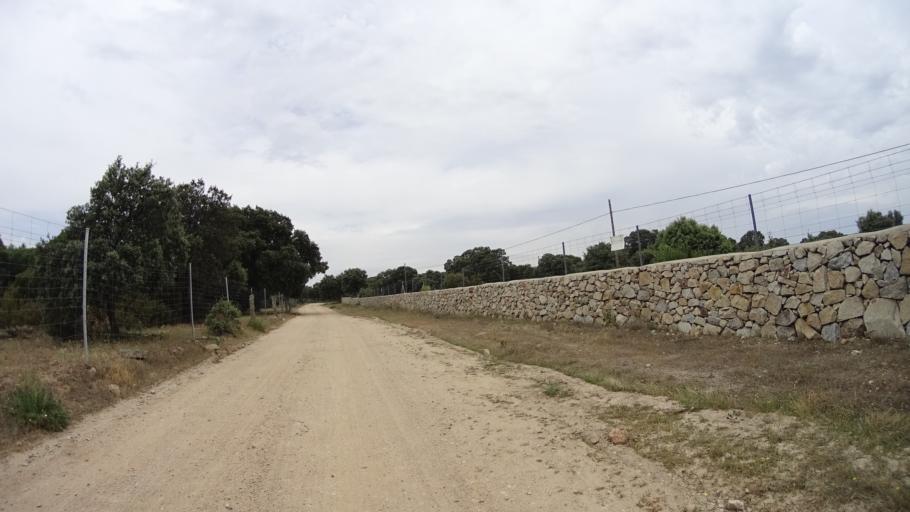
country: ES
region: Madrid
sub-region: Provincia de Madrid
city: Colmenarejo
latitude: 40.5452
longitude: -4.0360
